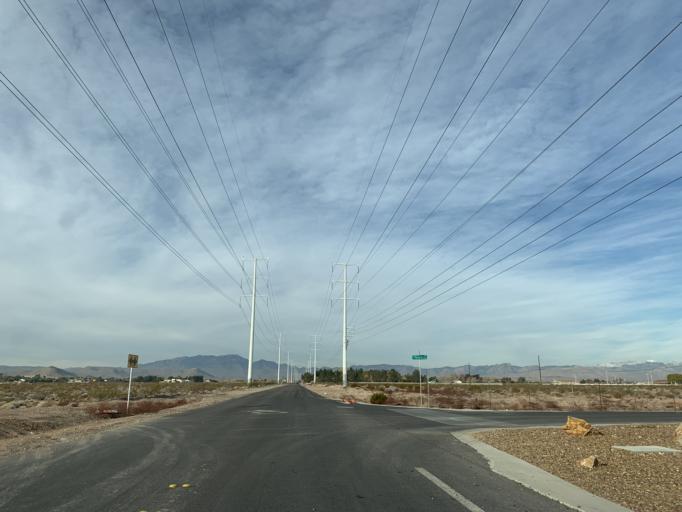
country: US
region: Nevada
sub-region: Clark County
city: Enterprise
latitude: 36.0028
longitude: -115.1852
